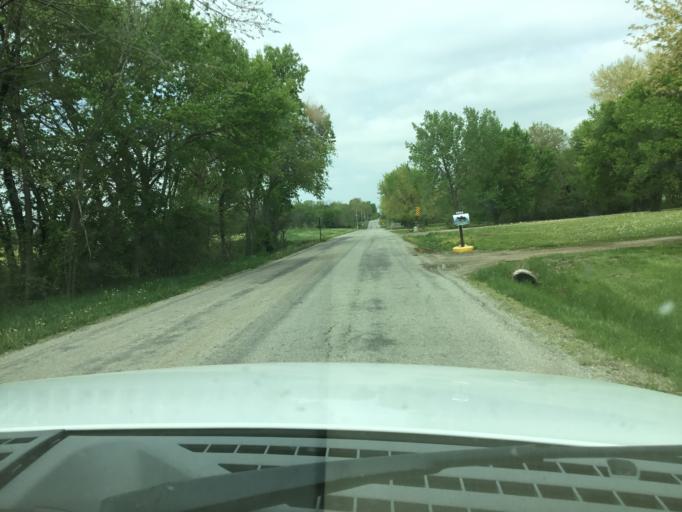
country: US
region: Kansas
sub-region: Shawnee County
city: Topeka
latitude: 38.9964
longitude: -95.5863
